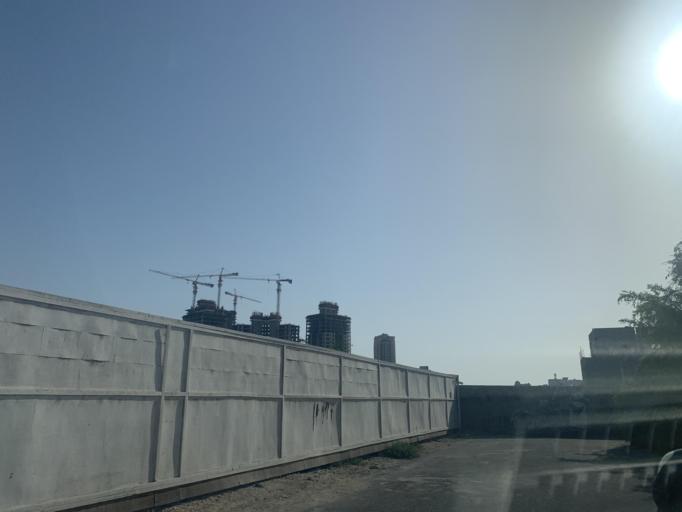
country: BH
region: Manama
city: Jidd Hafs
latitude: 26.2060
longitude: 50.4559
